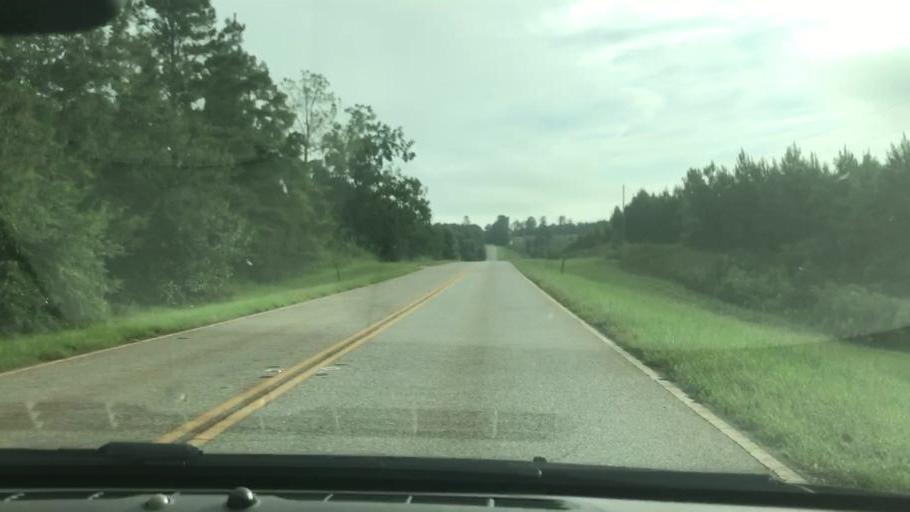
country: US
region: Georgia
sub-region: Quitman County
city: Georgetown
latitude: 31.9192
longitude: -85.0242
